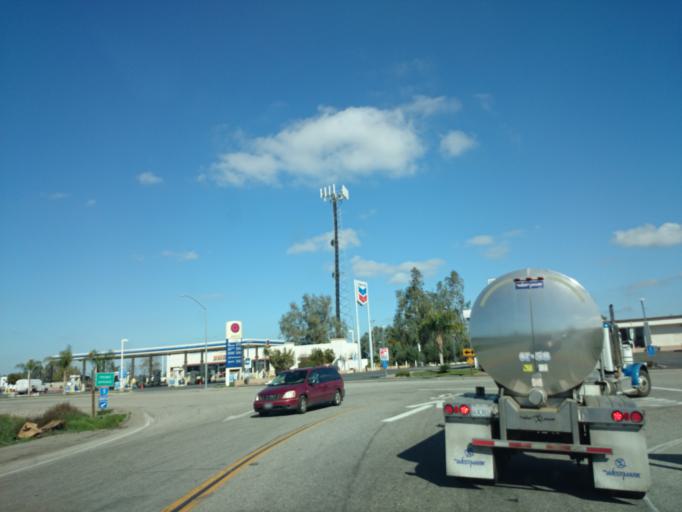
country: US
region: California
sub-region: Kern County
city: Buttonwillow
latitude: 35.4015
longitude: -119.3989
